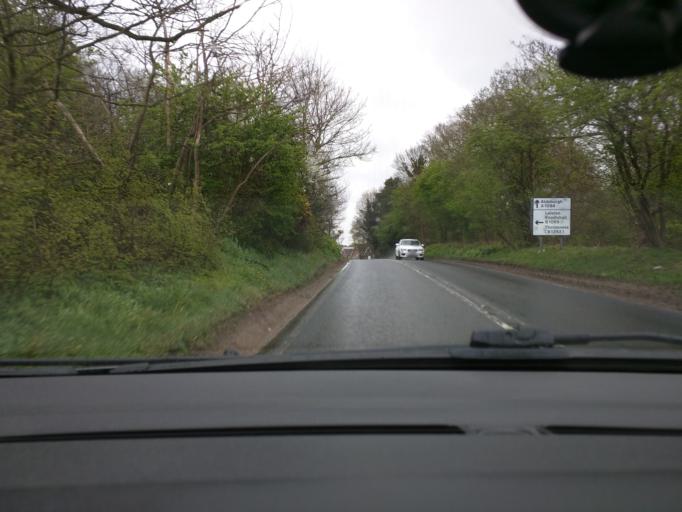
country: GB
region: England
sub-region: Suffolk
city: Leiston
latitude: 52.1797
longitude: 1.5363
